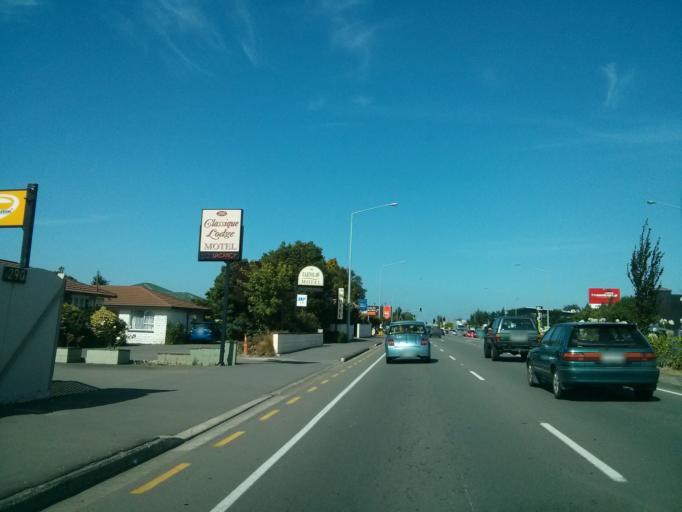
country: NZ
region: Canterbury
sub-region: Christchurch City
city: Christchurch
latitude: -43.5384
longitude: 172.5843
